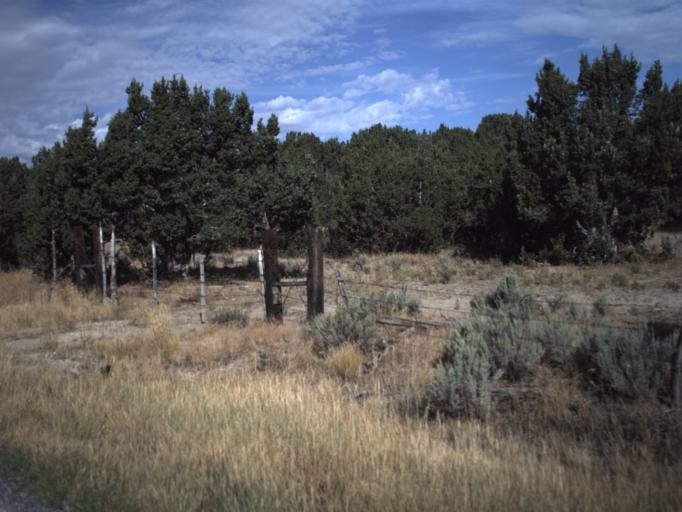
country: US
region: Idaho
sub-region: Cassia County
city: Burley
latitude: 41.8171
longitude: -113.2996
